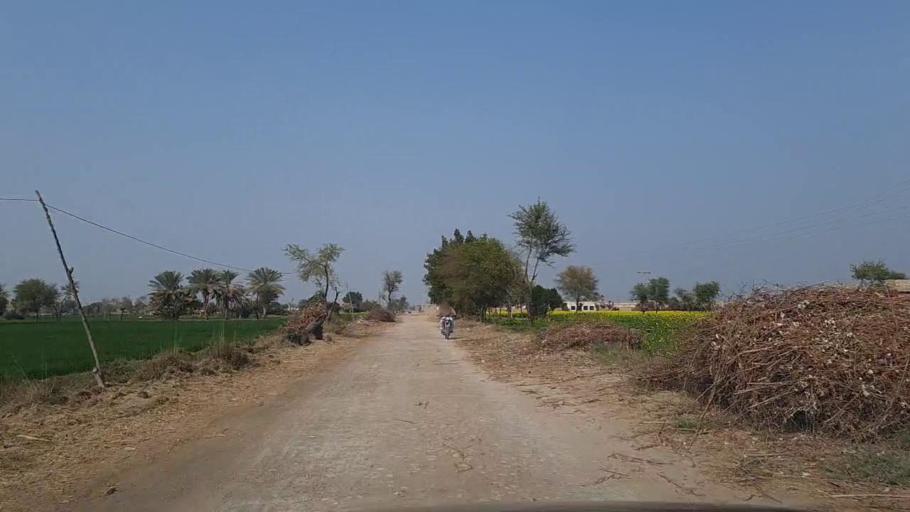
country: PK
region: Sindh
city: Daur
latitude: 26.4075
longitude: 68.4240
